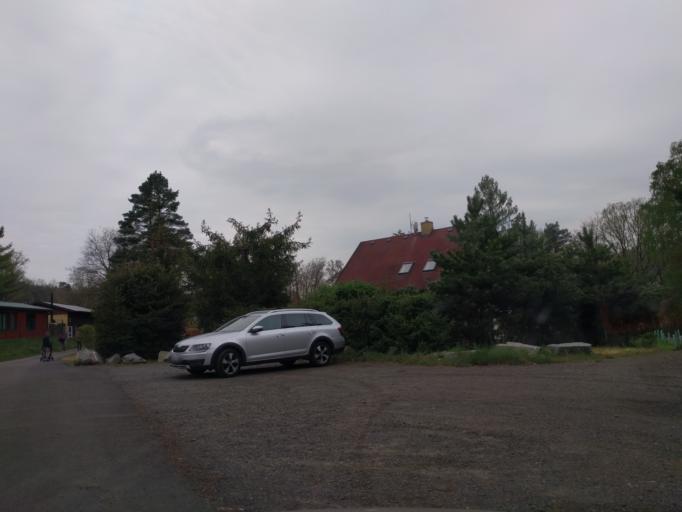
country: CZ
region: Central Bohemia
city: Krasna Hora nad Vltavou
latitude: 49.6650
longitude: 14.2567
